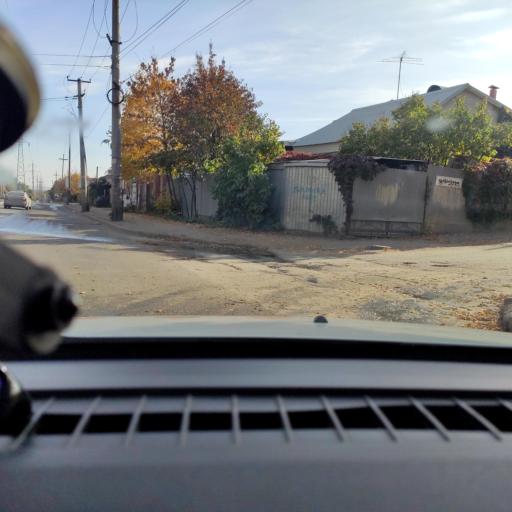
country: RU
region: Samara
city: Samara
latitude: 53.1969
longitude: 50.2145
